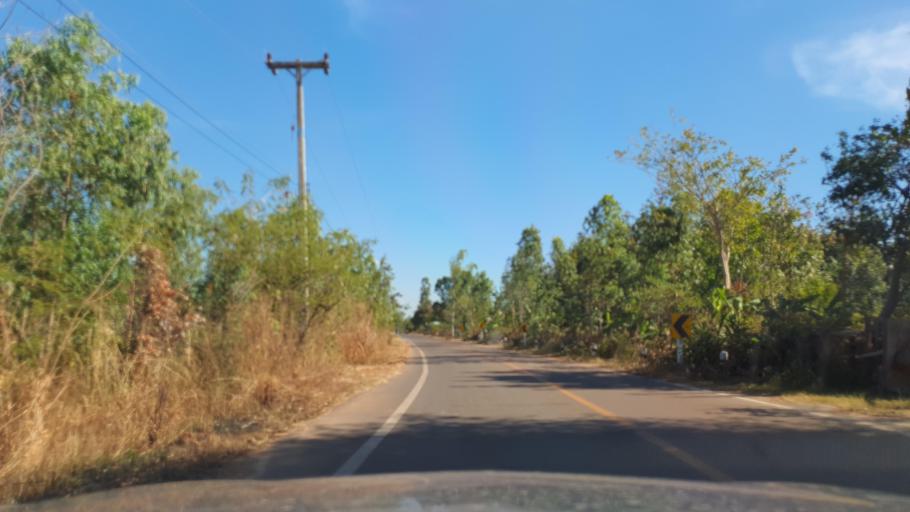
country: TH
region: Kalasin
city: Khao Wong
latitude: 16.6863
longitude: 104.1164
